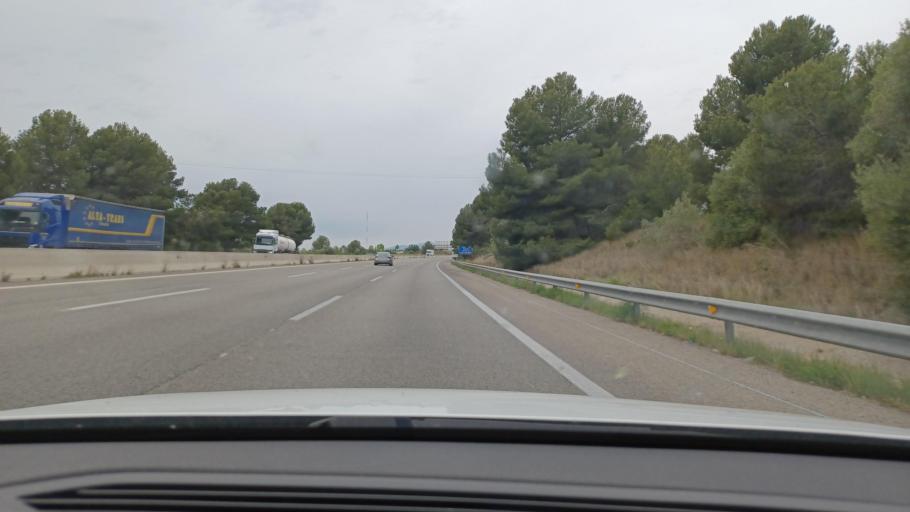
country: ES
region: Catalonia
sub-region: Provincia de Tarragona
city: Vila-seca
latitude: 41.1337
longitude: 1.1736
